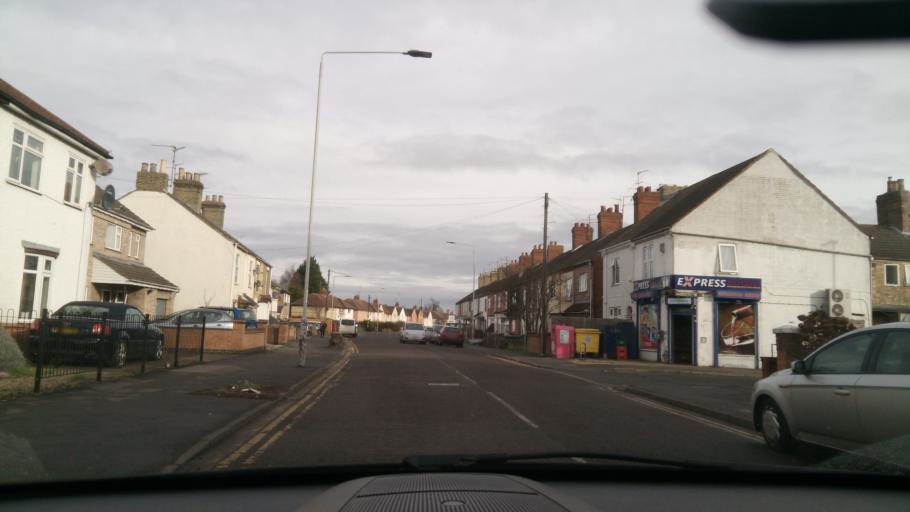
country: GB
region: England
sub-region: Peterborough
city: Peterborough
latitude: 52.5936
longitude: -0.2515
